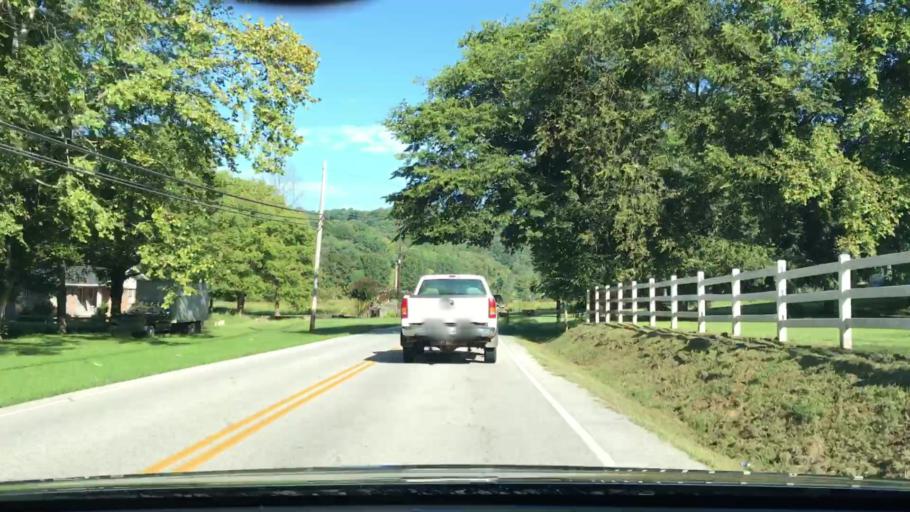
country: US
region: Tennessee
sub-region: Smith County
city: Carthage
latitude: 36.2869
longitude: -85.9492
